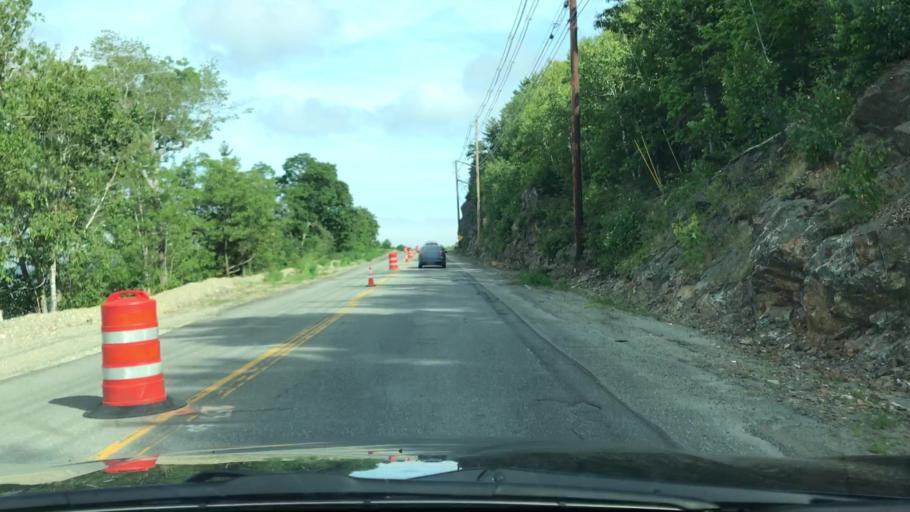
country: US
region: Maine
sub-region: Hancock County
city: Bar Harbor
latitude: 44.4082
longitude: -68.2394
